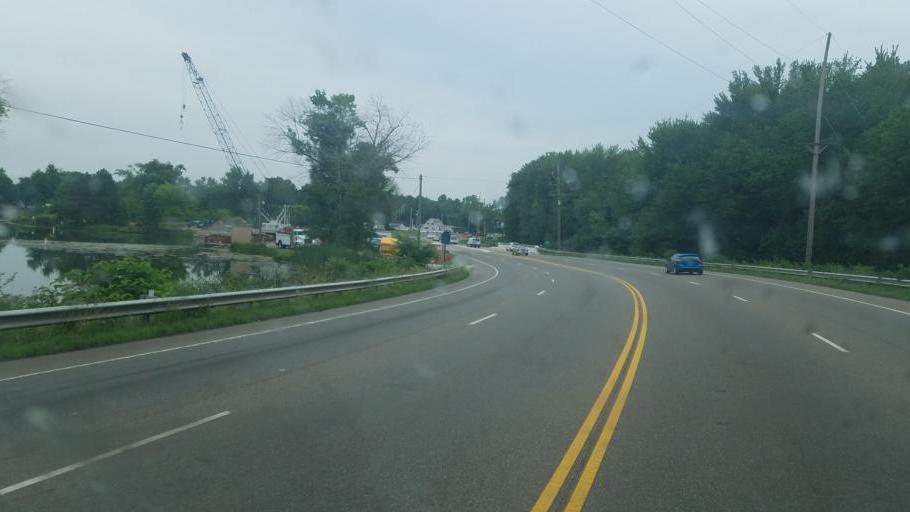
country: US
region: Ohio
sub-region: Summit County
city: Portage Lakes
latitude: 41.0230
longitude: -81.5502
